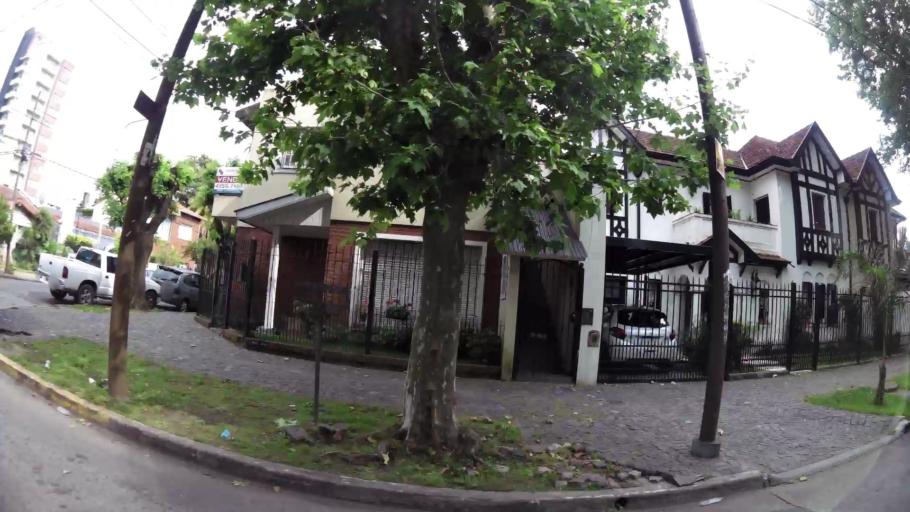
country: AR
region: Buenos Aires
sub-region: Partido de Quilmes
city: Quilmes
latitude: -34.7243
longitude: -58.2492
